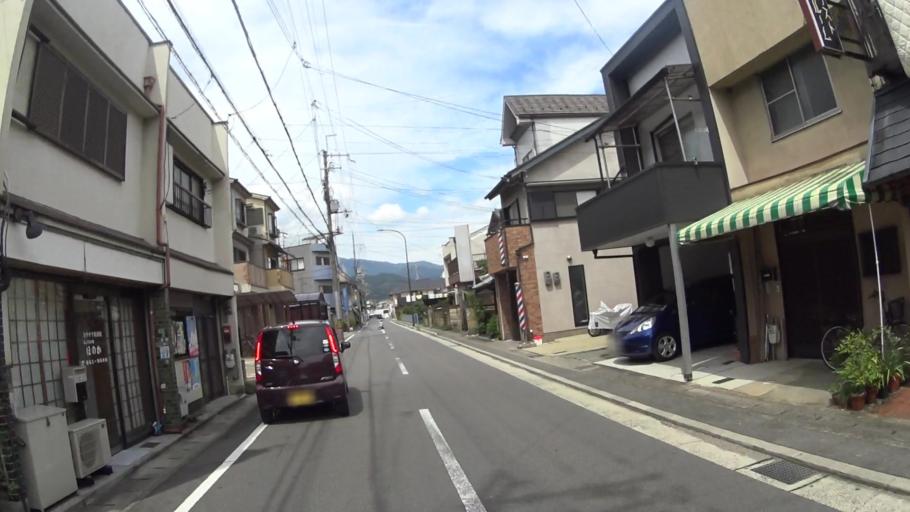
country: JP
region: Kyoto
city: Muko
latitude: 35.0084
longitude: 135.6816
